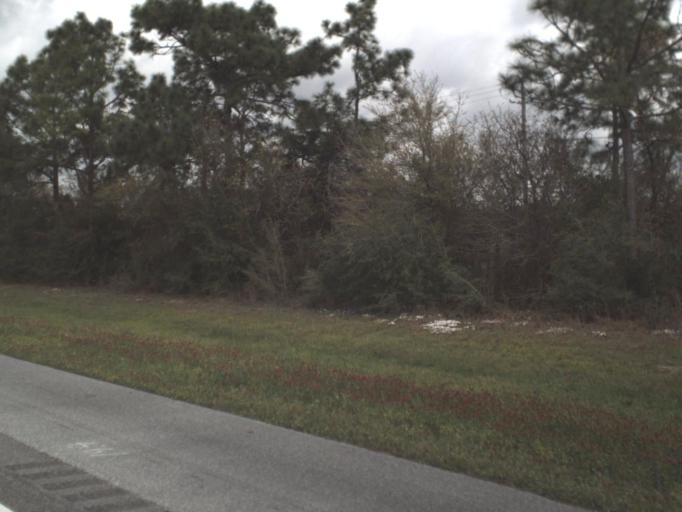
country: US
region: Florida
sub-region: Okaloosa County
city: Crestview
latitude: 30.7215
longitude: -86.4765
